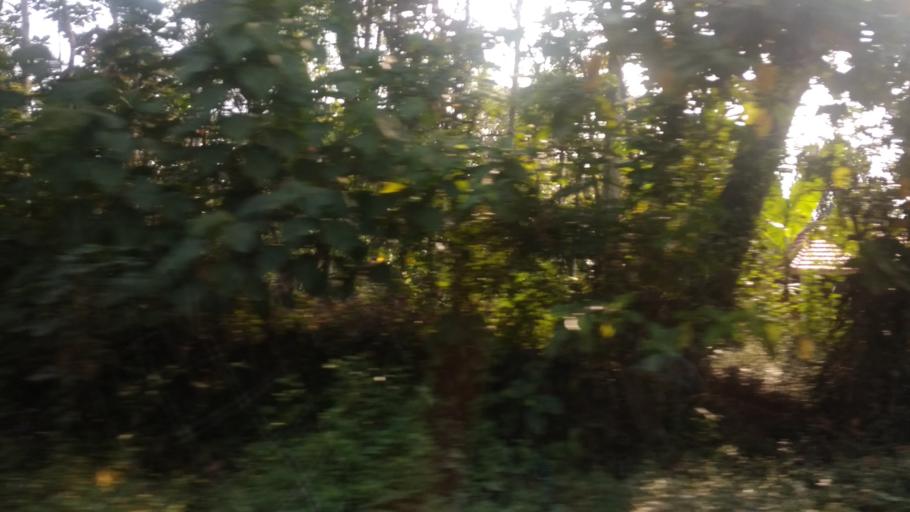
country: IN
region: Kerala
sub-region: Kottayam
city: Changanacheri
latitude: 9.5049
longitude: 76.6856
